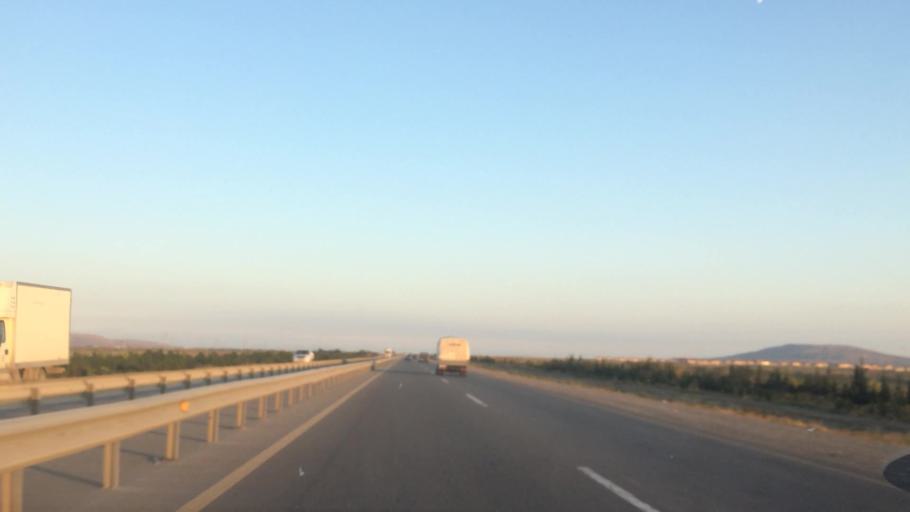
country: AZ
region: Baki
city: Qobustan
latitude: 39.9894
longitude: 49.2003
